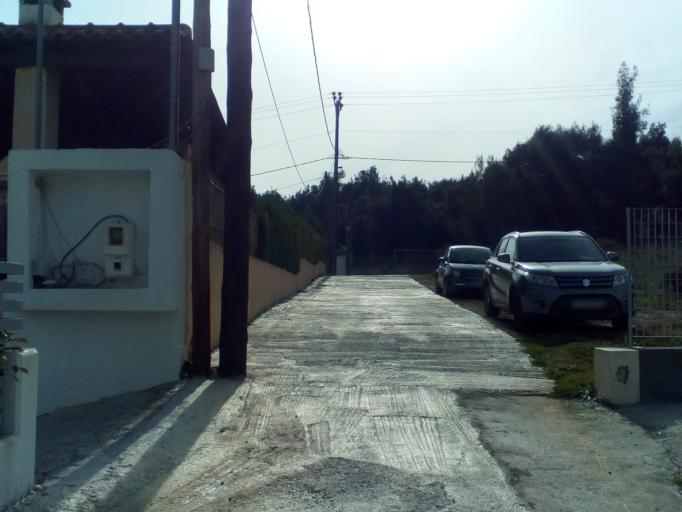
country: GR
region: Attica
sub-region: Nomarchia Anatolikis Attikis
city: Agios Stefanos
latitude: 38.1450
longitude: 23.8712
